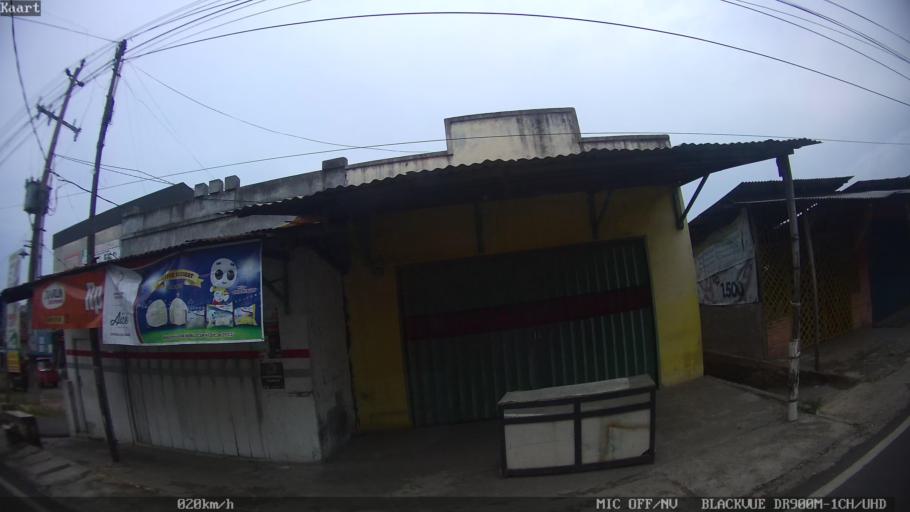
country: ID
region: Lampung
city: Bandarlampung
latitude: -5.4120
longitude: 105.2457
